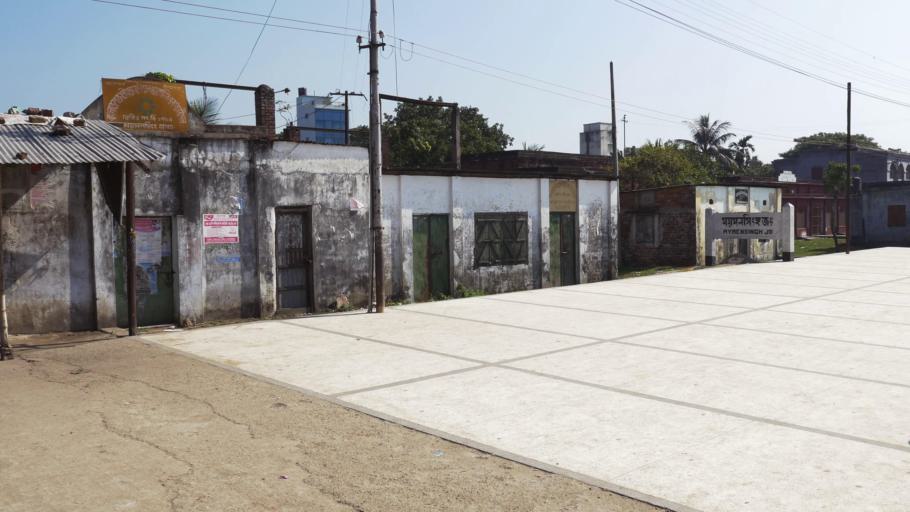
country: BD
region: Dhaka
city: Mymensingh
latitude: 24.6340
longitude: 90.4606
